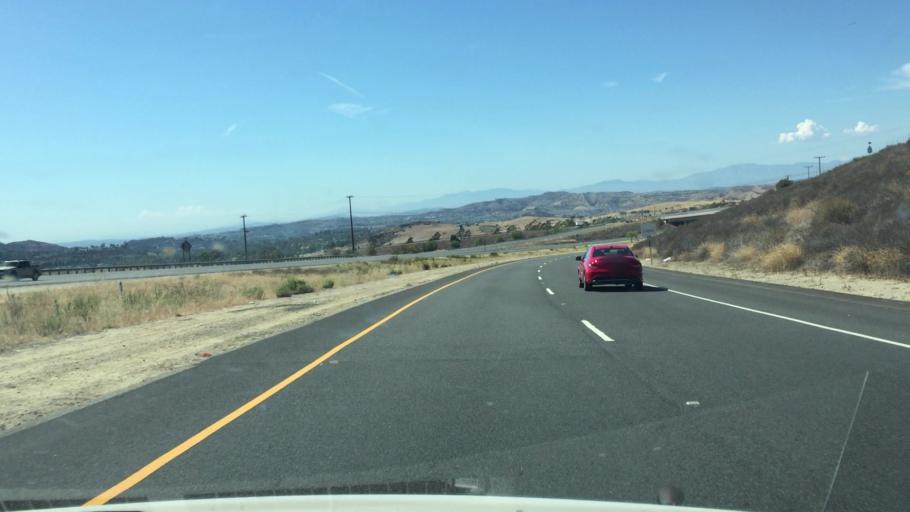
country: US
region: California
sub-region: Orange County
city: North Tustin
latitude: 33.7761
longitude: -117.7464
